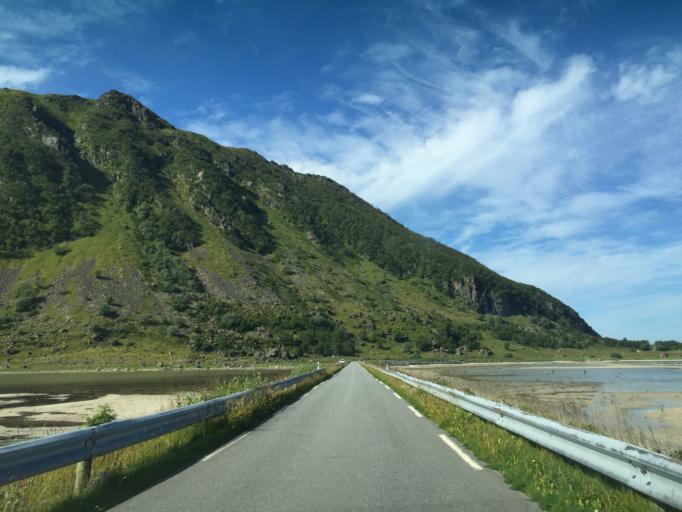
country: NO
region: Nordland
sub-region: Vagan
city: Svolvaer
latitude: 68.3952
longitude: 14.5459
